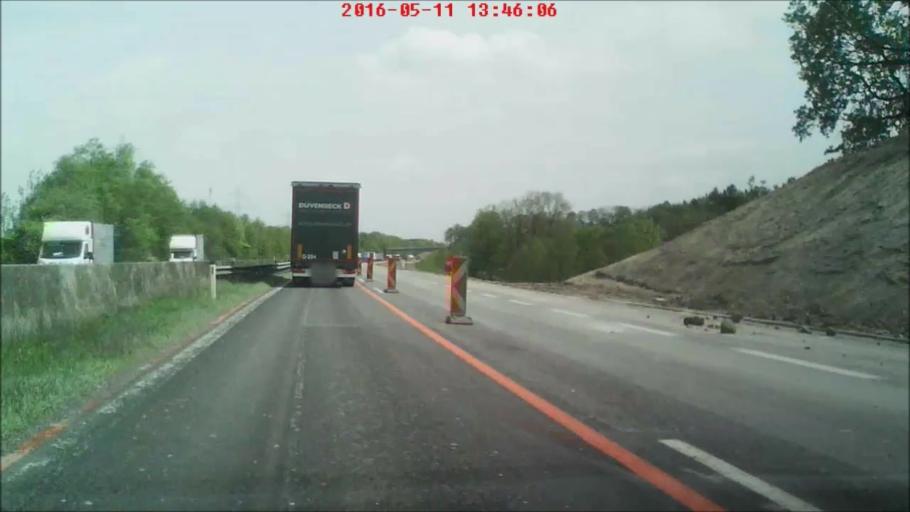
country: AT
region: Upper Austria
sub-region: Politischer Bezirk Vocklabruck
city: Wolfsegg am Hausruck
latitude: 48.2125
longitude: 13.6285
